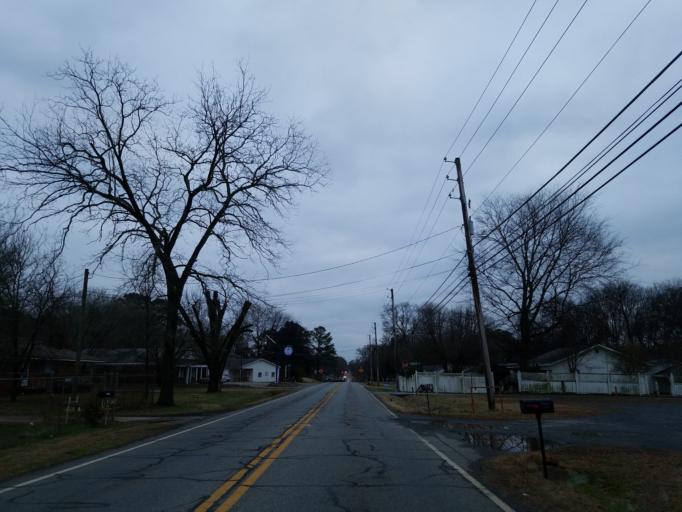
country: US
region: Georgia
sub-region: Bartow County
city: Cartersville
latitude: 34.2046
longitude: -84.8301
